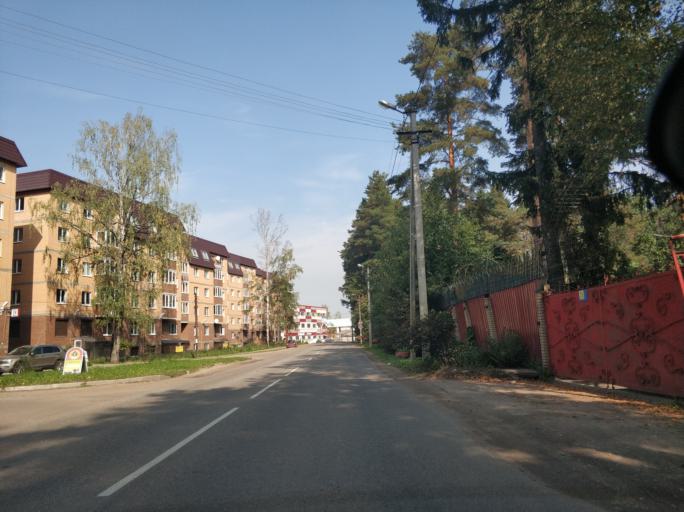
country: RU
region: Leningrad
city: Vsevolozhsk
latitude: 60.0156
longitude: 30.6230
